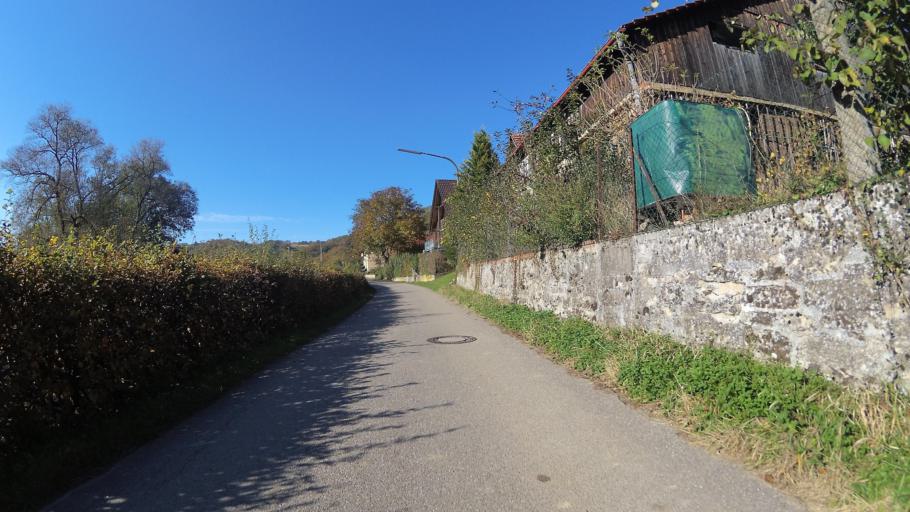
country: DE
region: Baden-Wuerttemberg
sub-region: Regierungsbezirk Stuttgart
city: Jagsthausen
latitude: 49.2820
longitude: 9.4751
